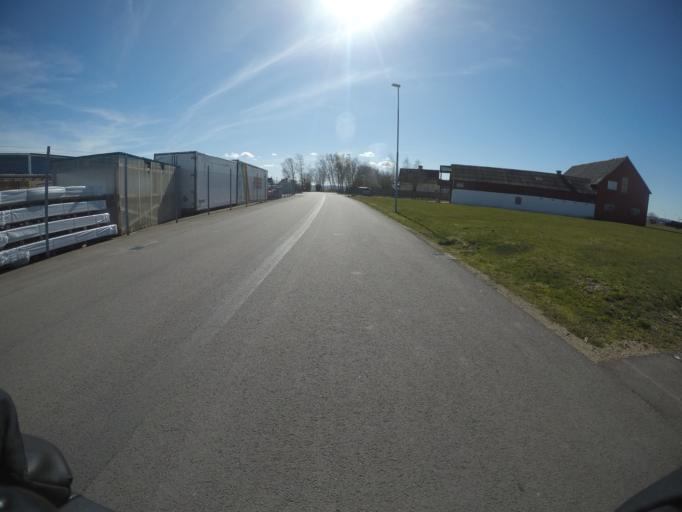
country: SE
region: Halland
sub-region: Laholms Kommun
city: Laholm
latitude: 56.4997
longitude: 13.0301
